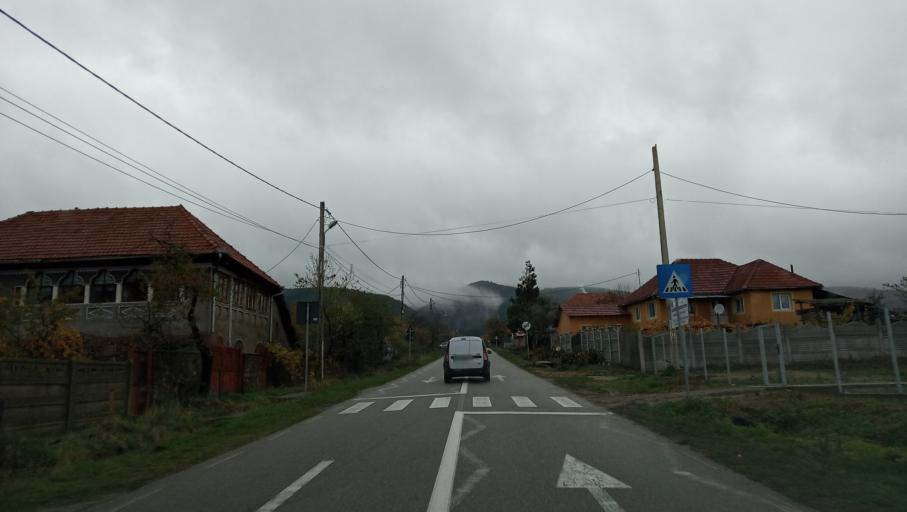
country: RO
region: Gorj
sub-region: Comuna Crasna
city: Crasna
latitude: 45.1705
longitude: 23.4840
